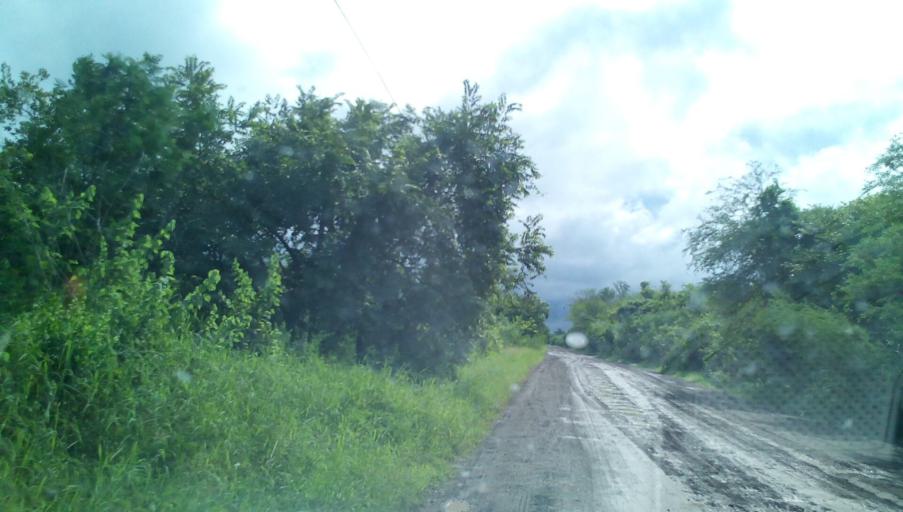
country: MX
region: Veracruz
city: Panuco
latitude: 21.8510
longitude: -98.1636
